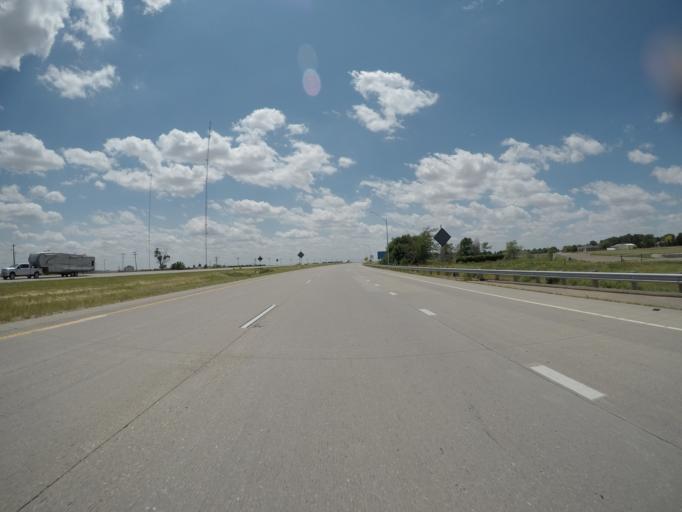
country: US
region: Colorado
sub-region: Kit Carson County
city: Burlington
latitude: 39.2982
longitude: -102.2596
